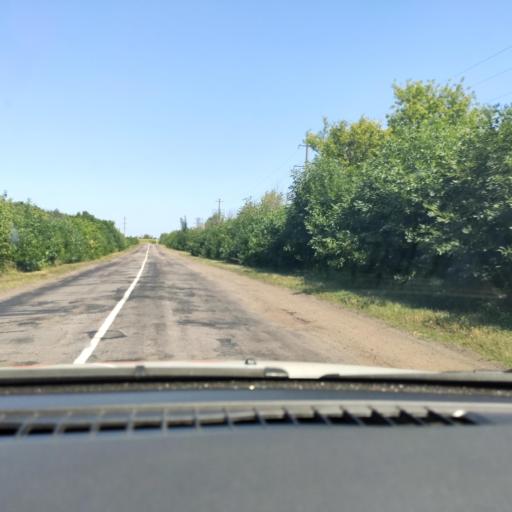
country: RU
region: Voronezj
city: Ol'khovatka
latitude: 50.6033
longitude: 39.3122
